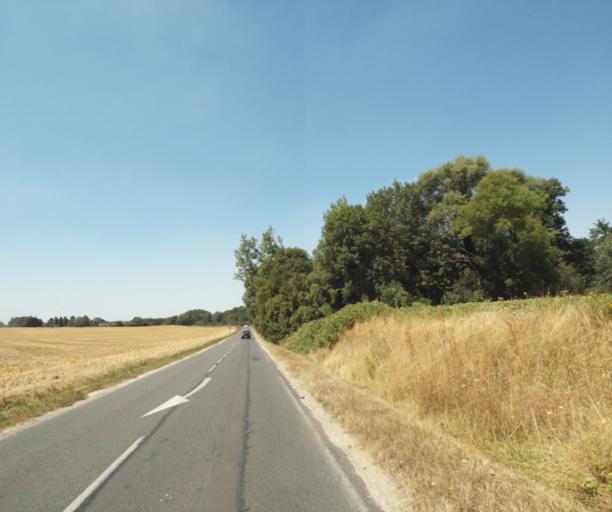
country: FR
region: Ile-de-France
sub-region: Departement de Seine-et-Marne
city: Chanteloup-en-Brie
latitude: 48.8511
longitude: 2.7333
